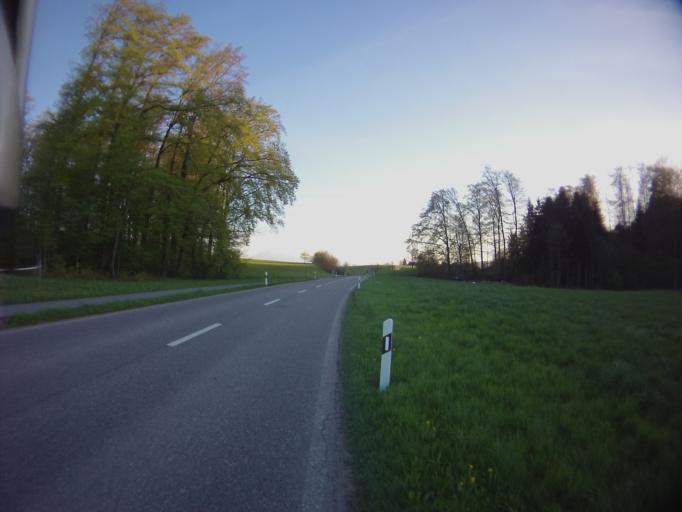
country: CH
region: Zurich
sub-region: Bezirk Affoltern
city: Mettmenstetten
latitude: 47.2402
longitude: 8.4530
